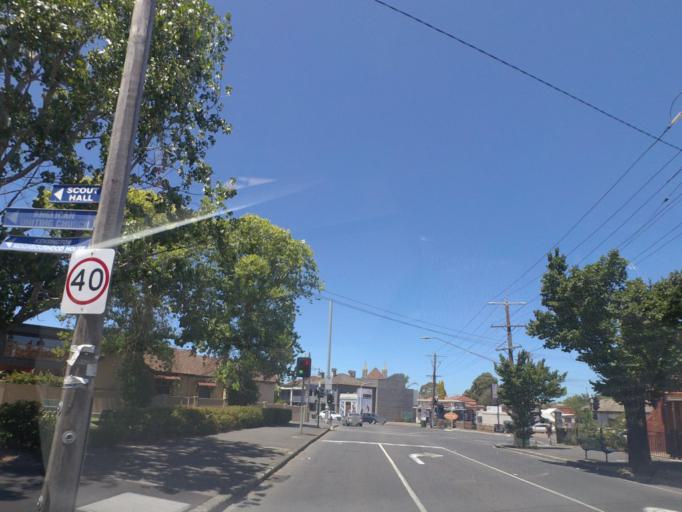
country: AU
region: Victoria
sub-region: Moonee Valley
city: Flemington
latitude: -37.7937
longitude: 144.9274
